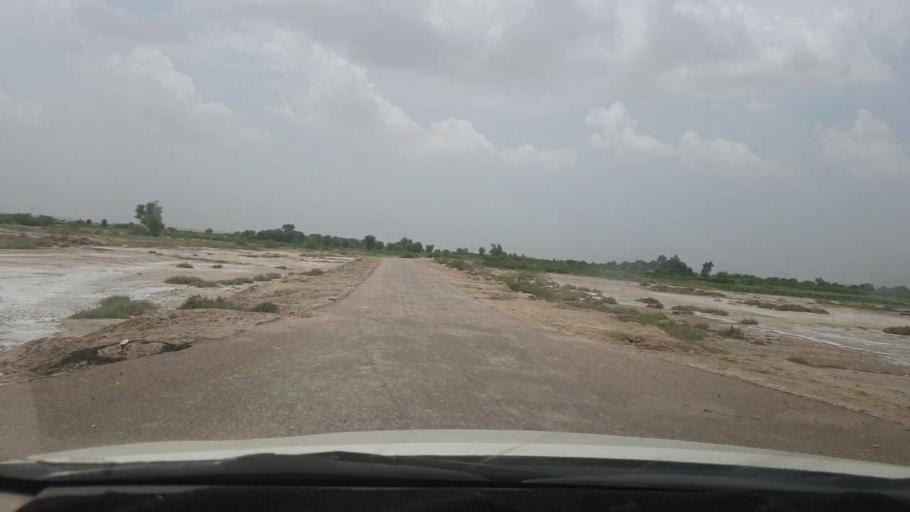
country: PK
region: Sindh
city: Khairpur
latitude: 27.3925
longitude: 68.9918
